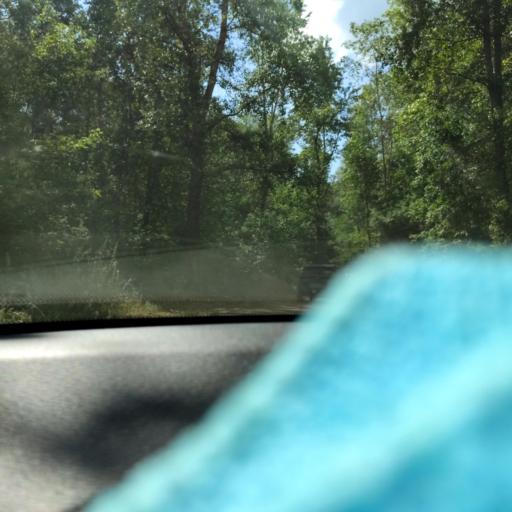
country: RU
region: Samara
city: Smyshlyayevka
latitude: 53.2211
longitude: 50.3439
